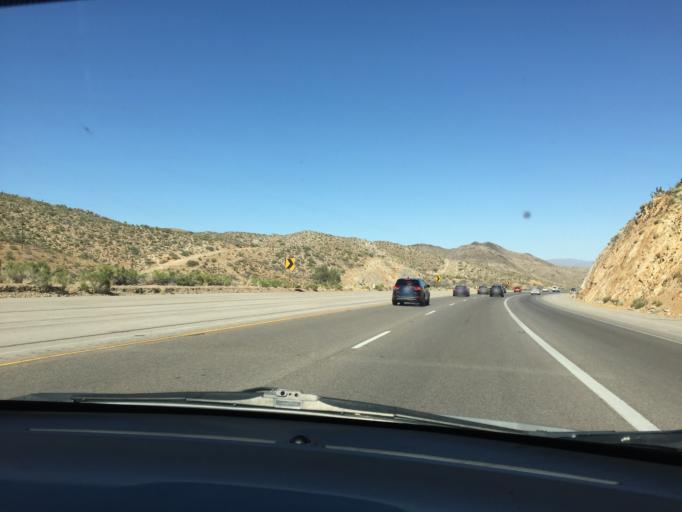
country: US
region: Nevada
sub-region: Clark County
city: Sandy Valley
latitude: 35.4702
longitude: -115.5047
